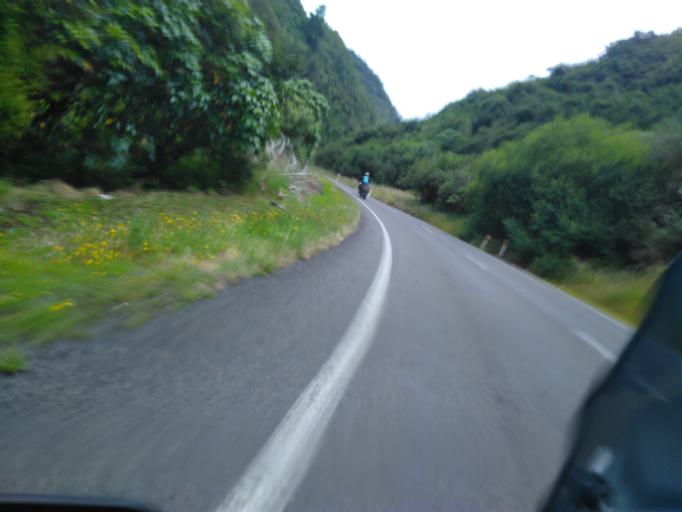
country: NZ
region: Bay of Plenty
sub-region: Opotiki District
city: Opotiki
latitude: -38.3412
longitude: 177.4317
